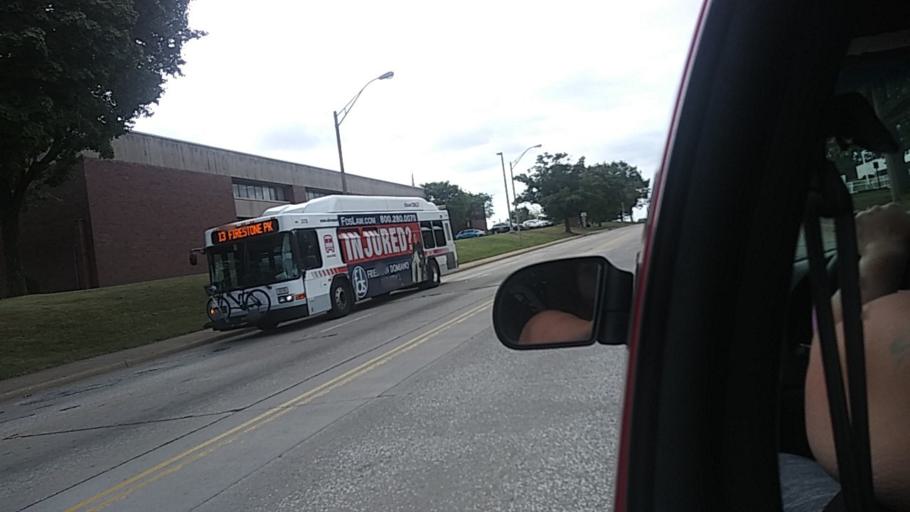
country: US
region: Ohio
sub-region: Summit County
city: Akron
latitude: 41.0657
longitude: -81.5205
